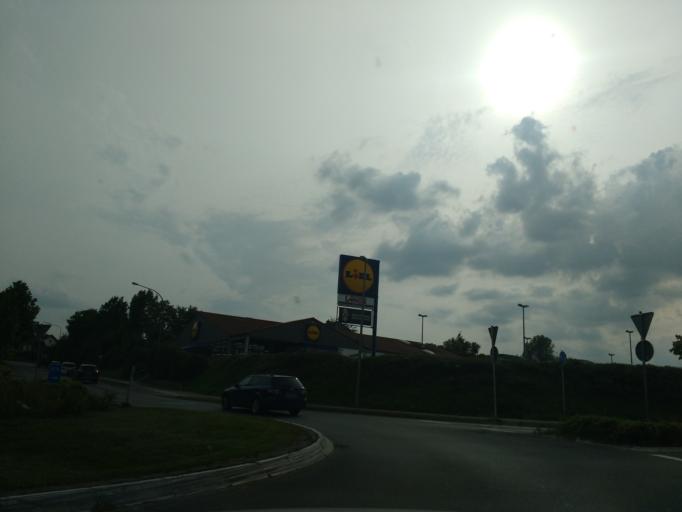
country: DE
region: North Rhine-Westphalia
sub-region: Regierungsbezirk Detmold
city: Paderborn
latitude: 51.6611
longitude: 8.7175
